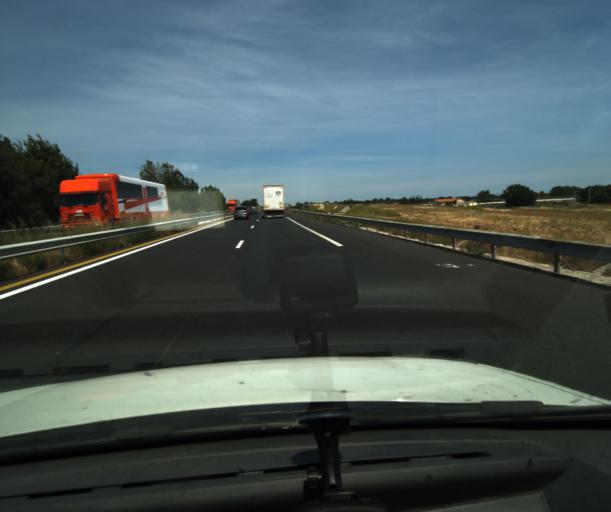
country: FR
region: Languedoc-Roussillon
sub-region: Departement des Pyrenees-Orientales
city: Saint-Esteve
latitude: 42.7077
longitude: 2.8674
